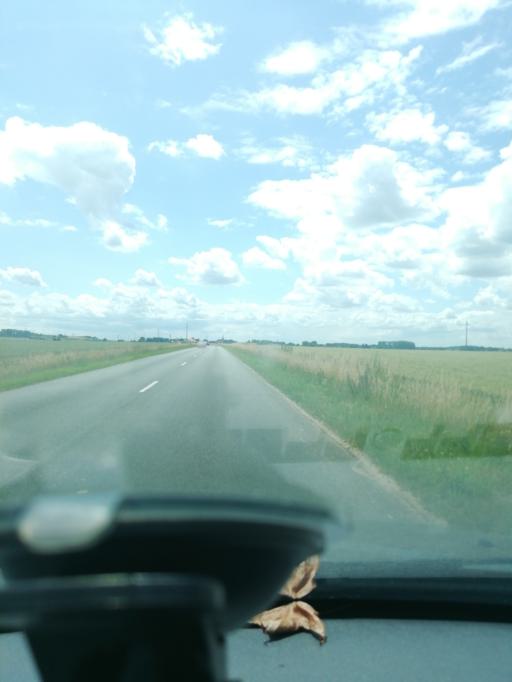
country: FR
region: Nord-Pas-de-Calais
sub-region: Departement du Nord
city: Cantin
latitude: 50.3239
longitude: 3.1454
